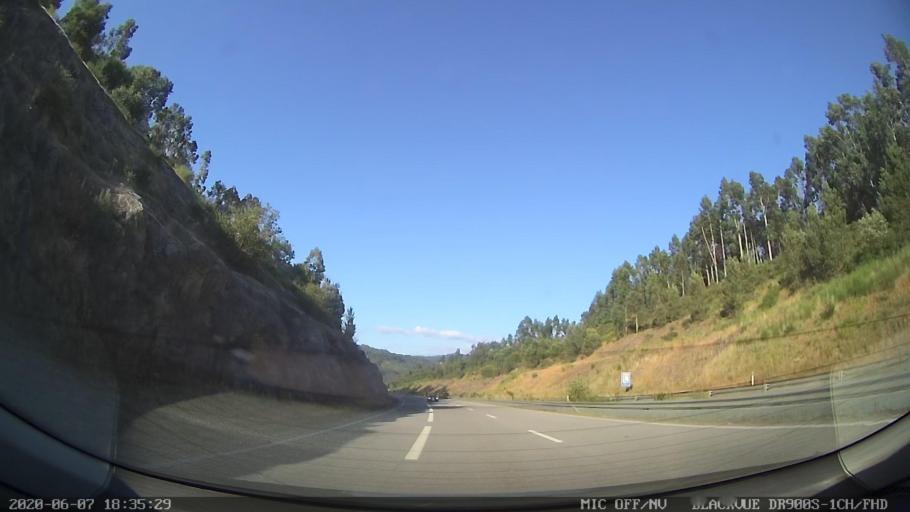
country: PT
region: Braga
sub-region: Guimaraes
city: Serzedo
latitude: 41.3983
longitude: -8.2357
